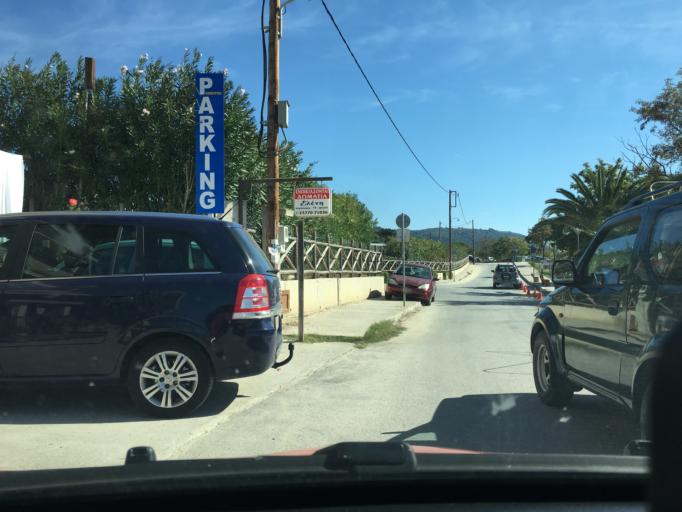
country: GR
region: Central Macedonia
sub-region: Nomos Chalkidikis
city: Ouranoupolis
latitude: 40.3245
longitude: 23.9827
